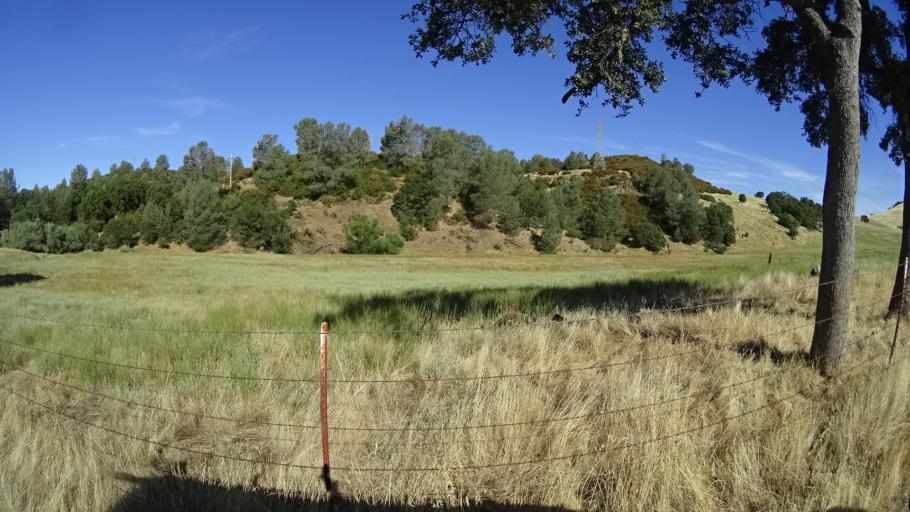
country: US
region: California
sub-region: Calaveras County
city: Valley Springs
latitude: 38.2171
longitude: -120.7855
